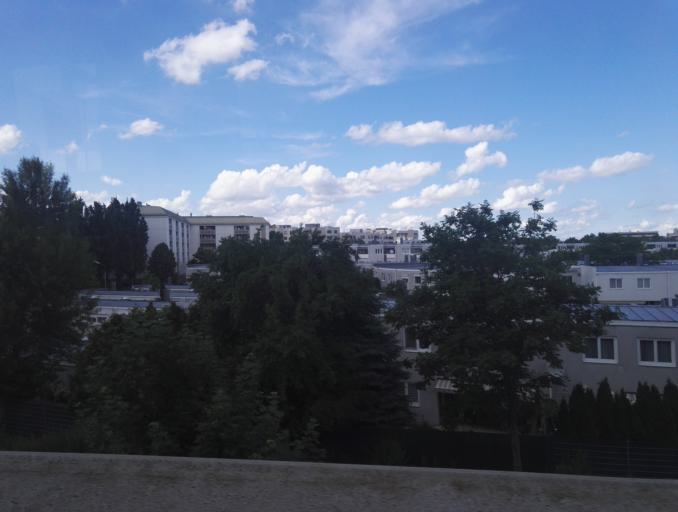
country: AT
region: Lower Austria
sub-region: Politischer Bezirk Wien-Umgebung
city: Gerasdorf bei Wien
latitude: 48.2193
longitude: 16.4679
